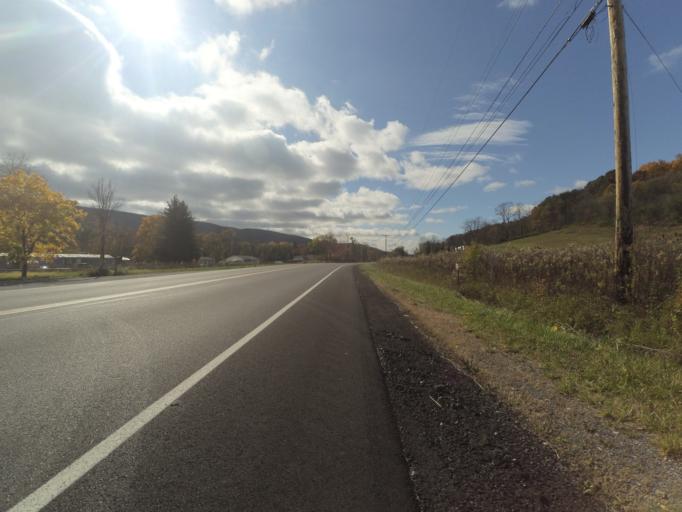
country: US
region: Pennsylvania
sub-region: Centre County
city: Park Forest Village
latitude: 40.8634
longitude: -77.9429
